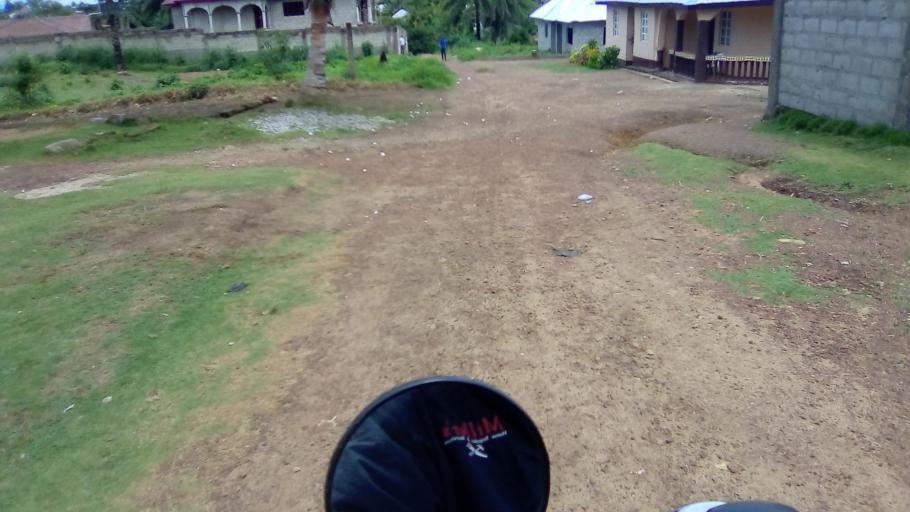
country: SL
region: Southern Province
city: Bo
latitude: 7.9316
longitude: -11.7209
